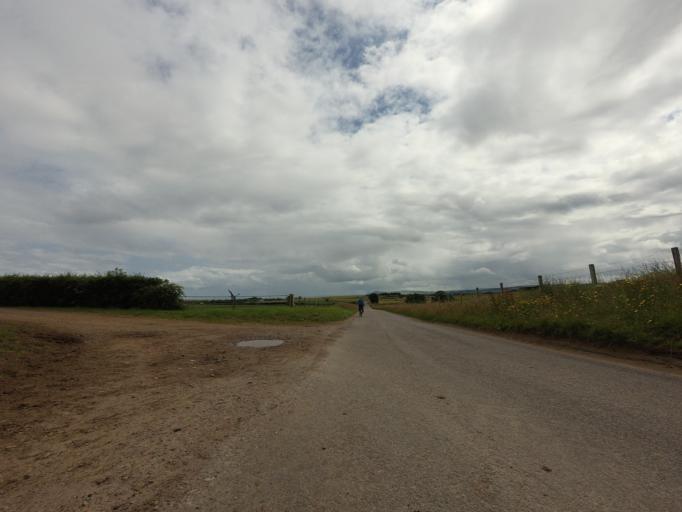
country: GB
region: Scotland
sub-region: Moray
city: Fochabers
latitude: 57.6674
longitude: -3.1372
